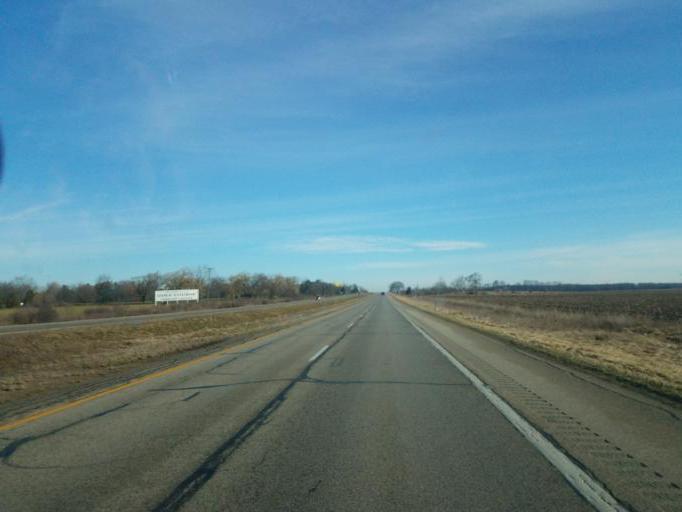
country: US
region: Michigan
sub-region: Gratiot County
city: Ithaca
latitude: 43.2205
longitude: -84.5631
